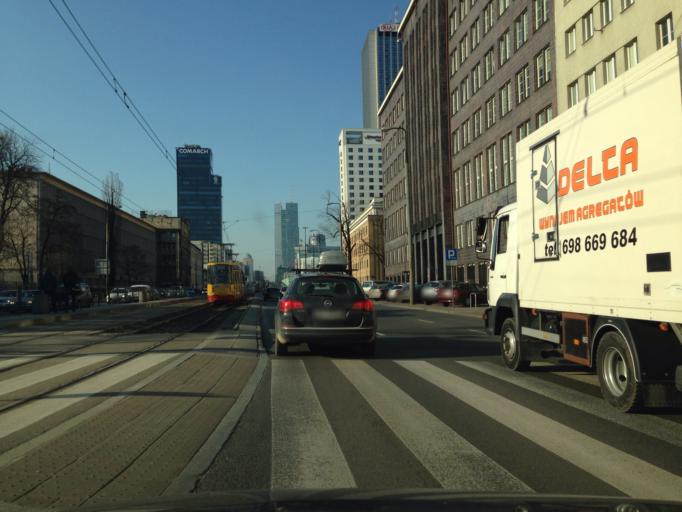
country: PL
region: Masovian Voivodeship
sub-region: Warszawa
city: Warsaw
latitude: 52.2231
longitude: 21.0048
